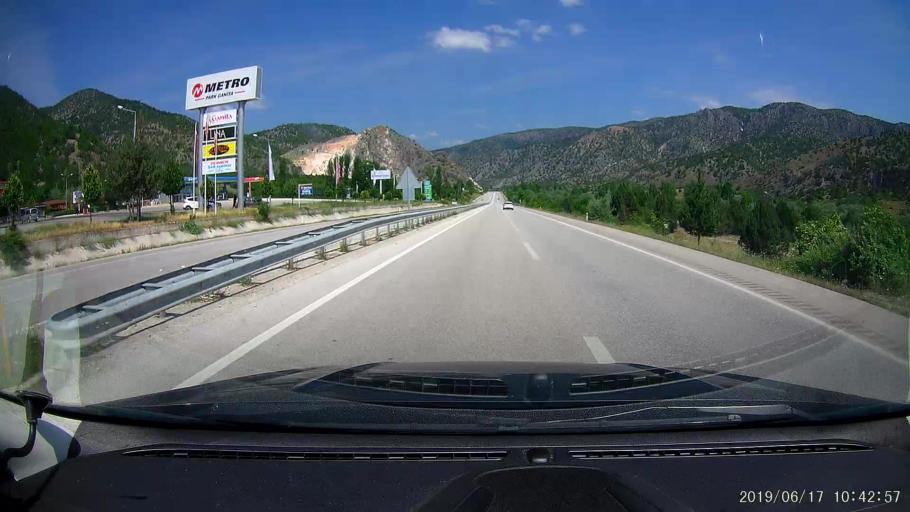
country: TR
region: Corum
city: Kargi
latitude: 41.0557
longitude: 34.5440
